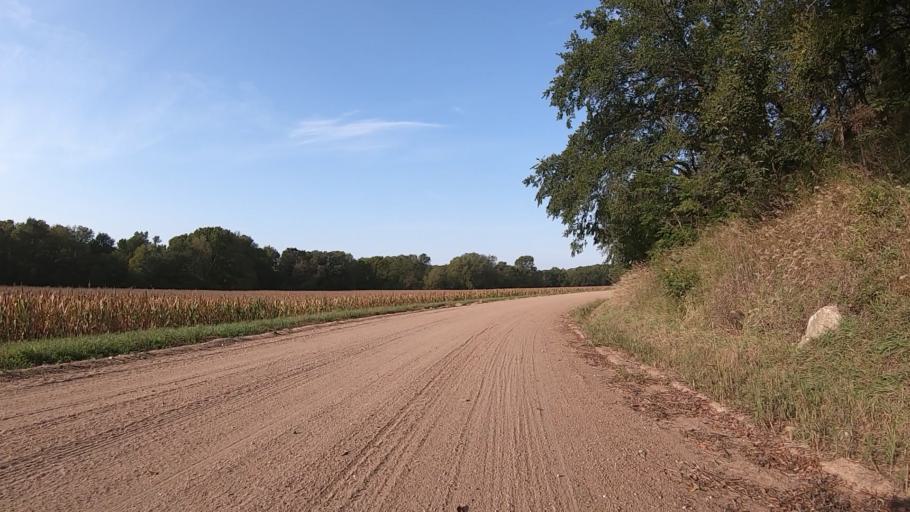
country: US
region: Kansas
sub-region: Marshall County
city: Blue Rapids
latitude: 39.6627
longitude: -96.8173
